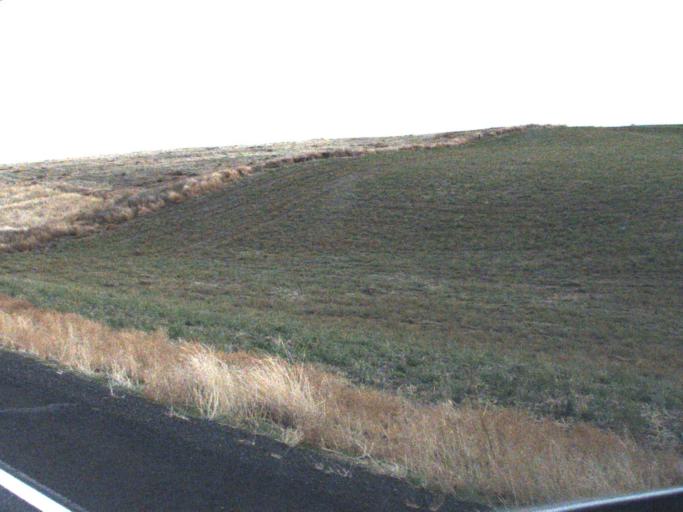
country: US
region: Washington
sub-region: Walla Walla County
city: Garrett
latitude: 46.0532
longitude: -118.7114
